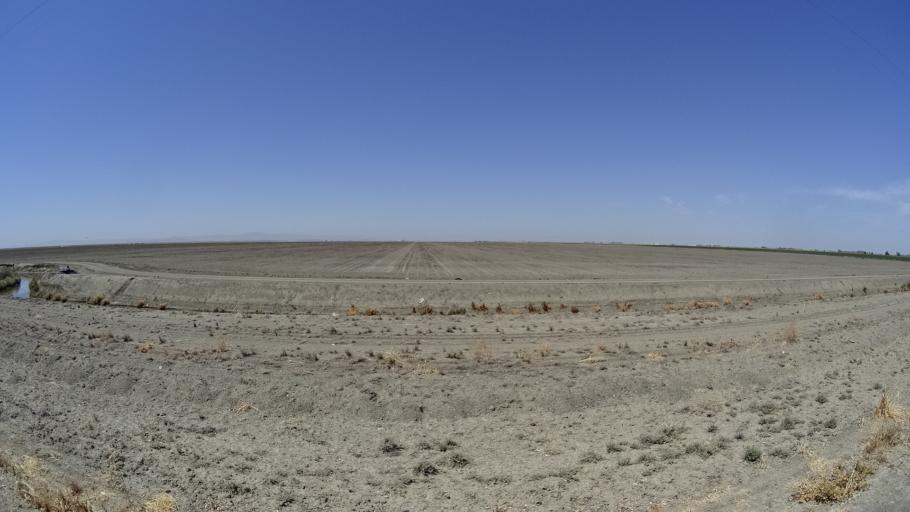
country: US
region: California
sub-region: Kings County
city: Stratford
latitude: 36.1287
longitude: -119.7340
